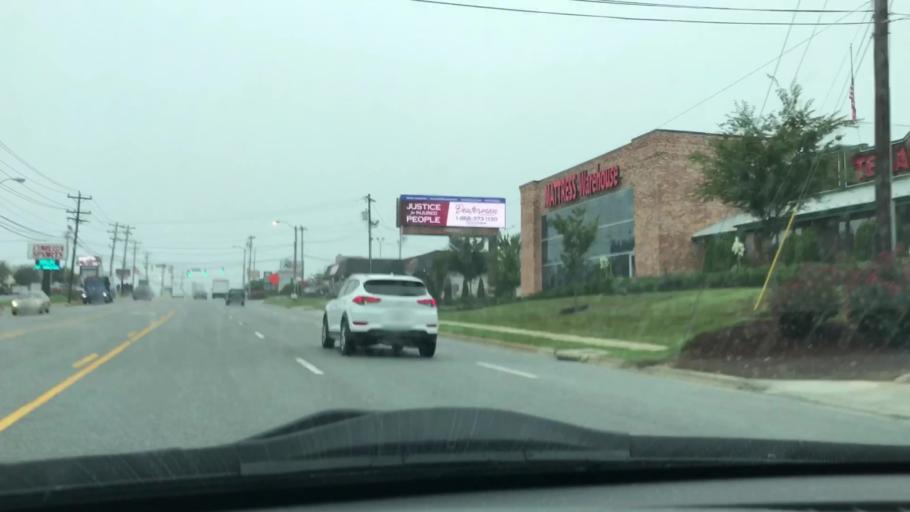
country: US
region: North Carolina
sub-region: Guilford County
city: Greensboro
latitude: 36.1023
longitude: -79.8236
